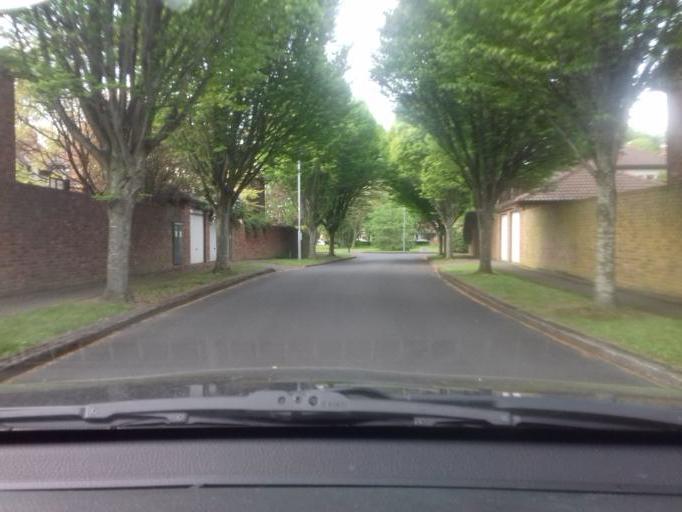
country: IE
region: Leinster
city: Castleknock
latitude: 53.3714
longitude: -6.3436
